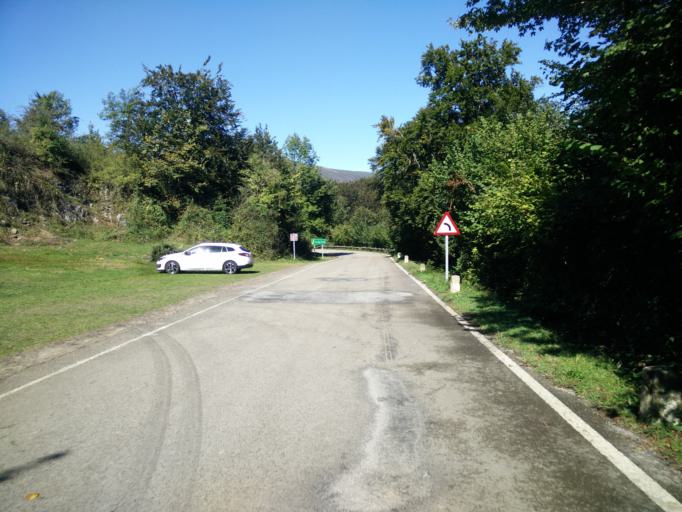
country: ES
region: Cantabria
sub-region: Provincia de Cantabria
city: Ruente
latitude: 43.1125
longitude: -4.2848
